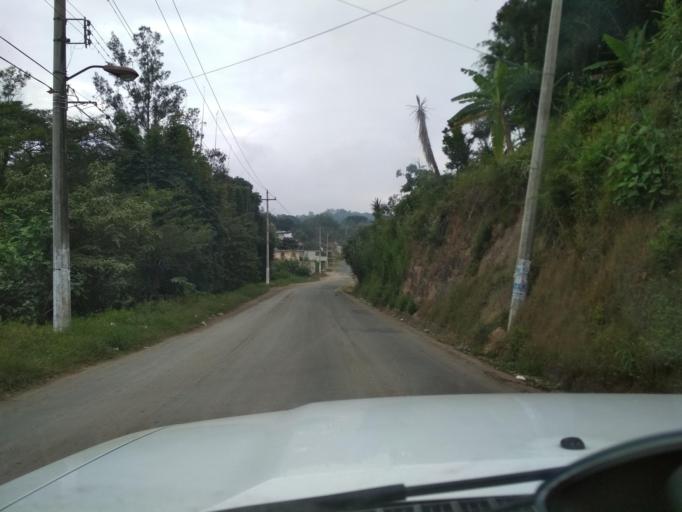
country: MX
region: Veracruz
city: El Castillo
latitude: 19.5636
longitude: -96.8605
